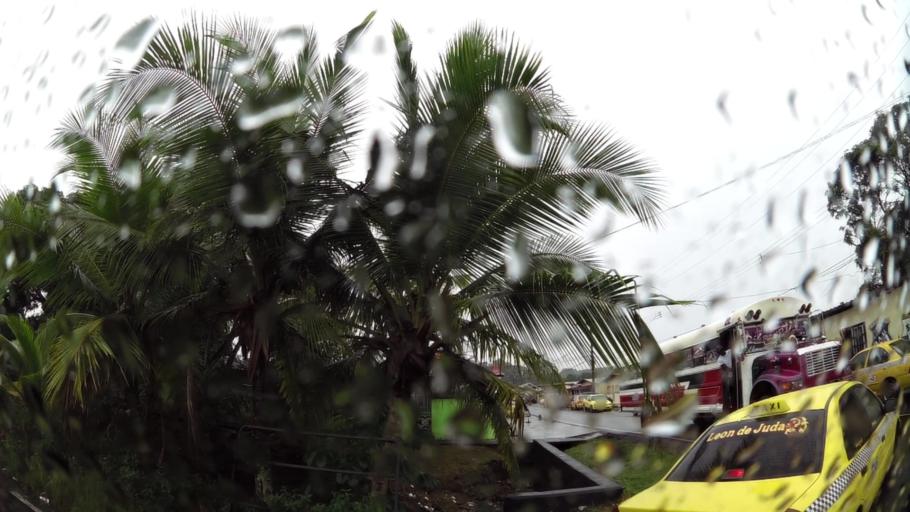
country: PA
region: Colon
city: Sabanitas
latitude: 9.3541
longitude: -79.8057
